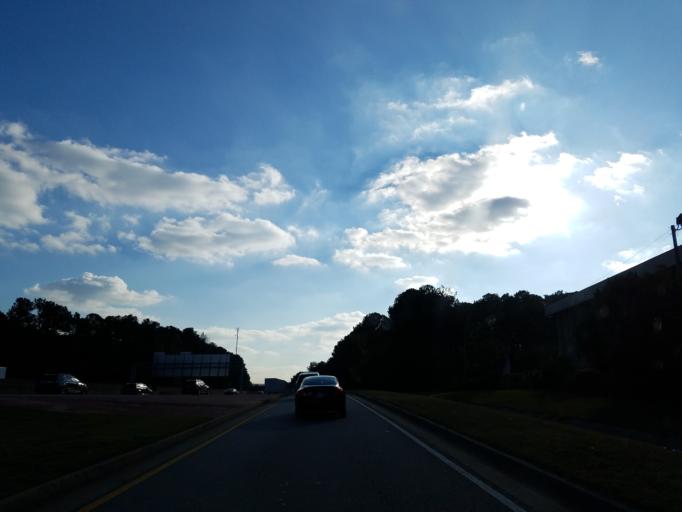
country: US
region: Georgia
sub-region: Cobb County
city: Vinings
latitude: 33.8833
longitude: -84.4717
